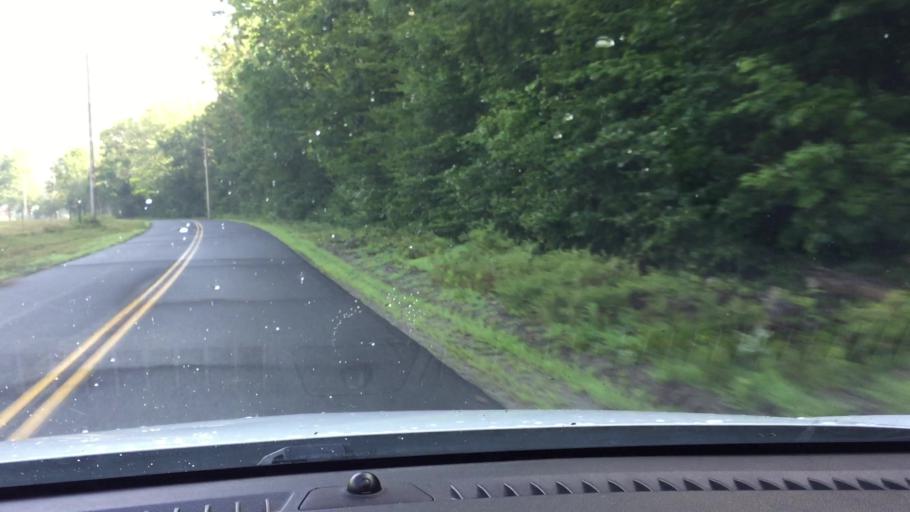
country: US
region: Massachusetts
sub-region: Berkshire County
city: Becket
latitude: 42.3937
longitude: -72.9776
